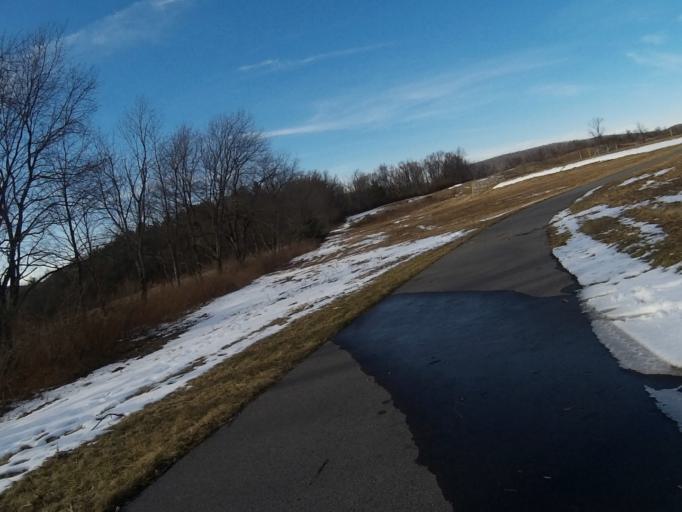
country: US
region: Pennsylvania
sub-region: Centre County
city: Houserville
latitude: 40.8482
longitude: -77.8773
